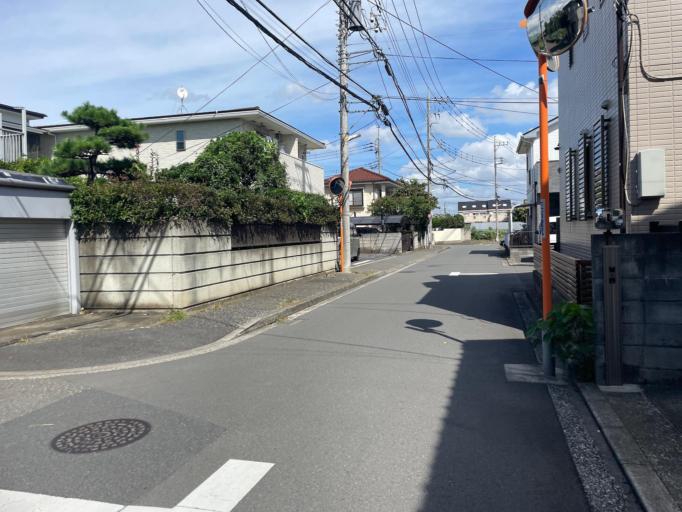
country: JP
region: Tokyo
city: Tanashicho
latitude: 35.7547
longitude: 139.5247
